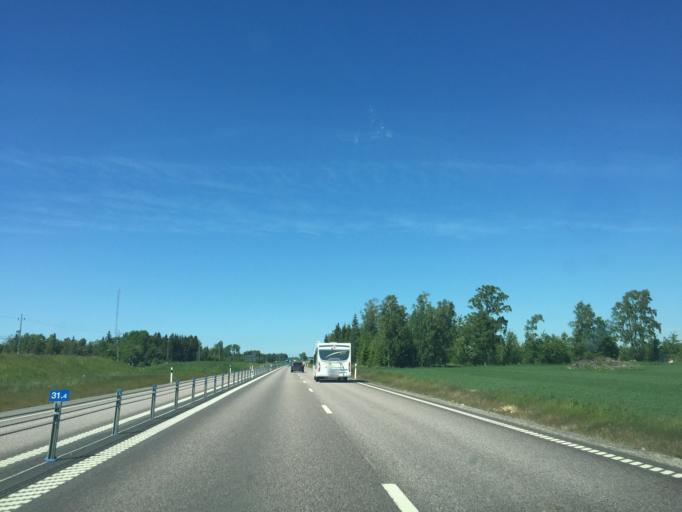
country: SE
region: OEstergoetland
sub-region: Motala Kommun
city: Stenstorp
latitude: 58.4111
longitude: 15.0790
